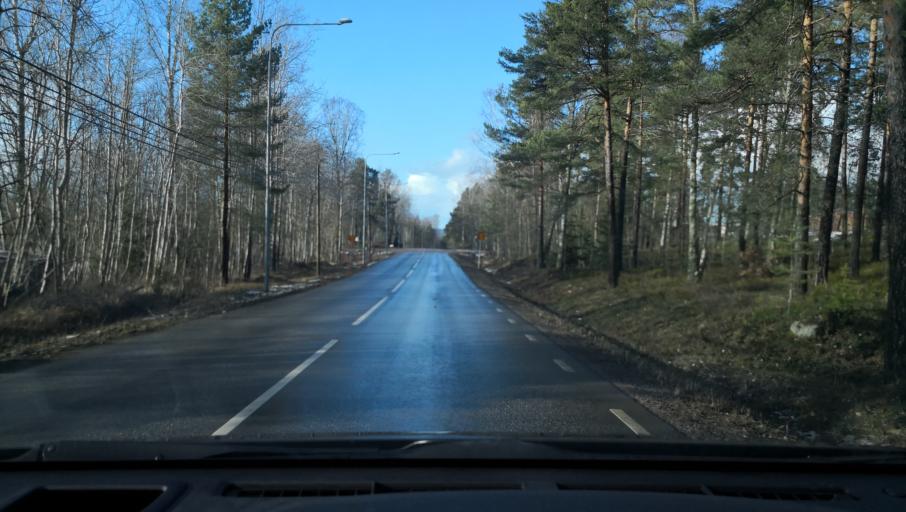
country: SE
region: Vaestmanland
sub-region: Arboga Kommun
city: Arboga
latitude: 59.3775
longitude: 15.8414
